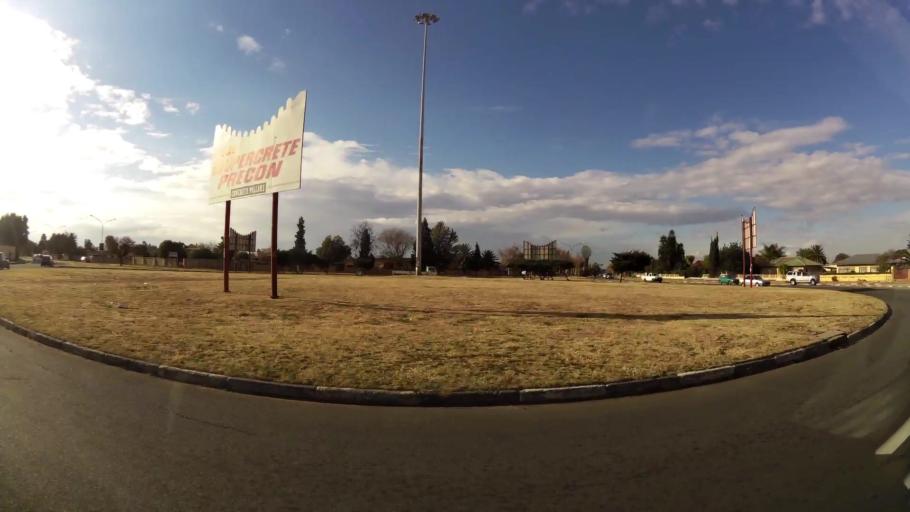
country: ZA
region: Orange Free State
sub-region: Lejweleputswa District Municipality
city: Welkom
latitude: -27.9931
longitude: 26.7486
